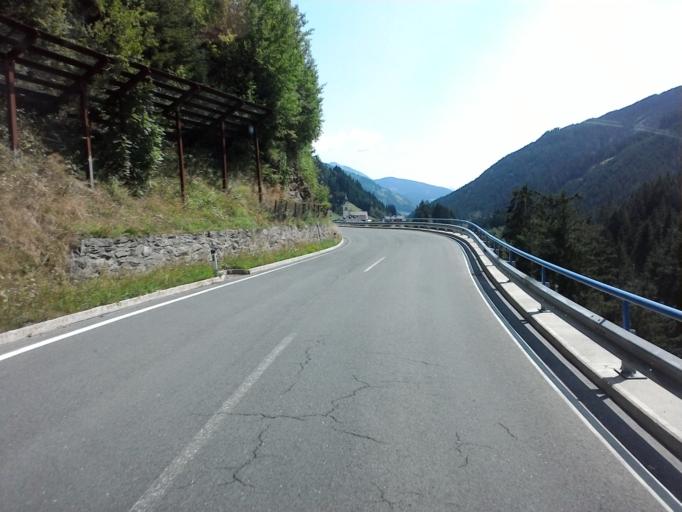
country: AT
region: Tyrol
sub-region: Politischer Bezirk Lienz
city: Untertilliach
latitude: 46.7032
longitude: 12.6714
